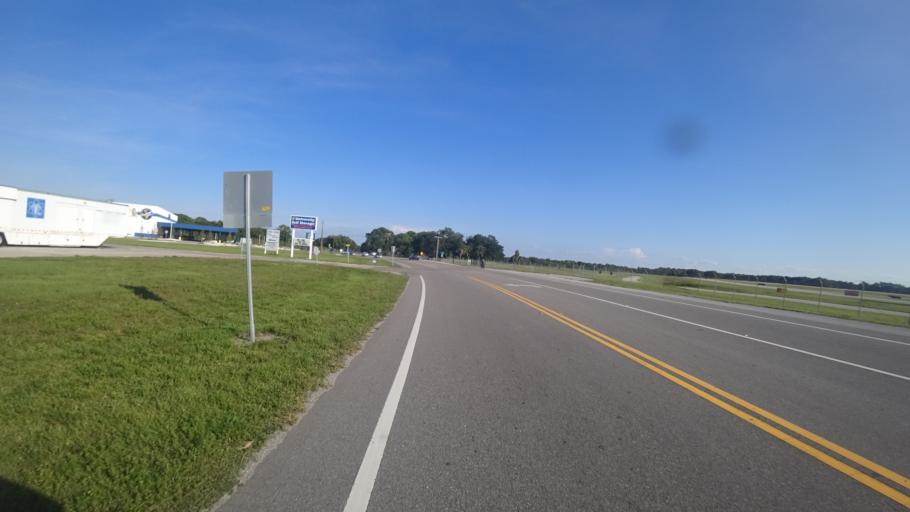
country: US
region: Florida
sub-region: Manatee County
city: Whitfield
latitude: 27.3895
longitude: -82.5451
